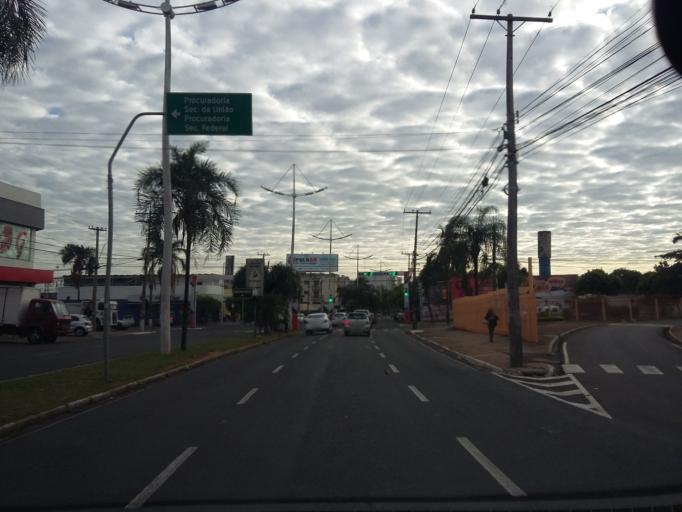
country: BR
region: Sao Paulo
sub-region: Sao Jose Do Rio Preto
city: Sao Jose do Rio Preto
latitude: -20.8337
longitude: -49.3998
